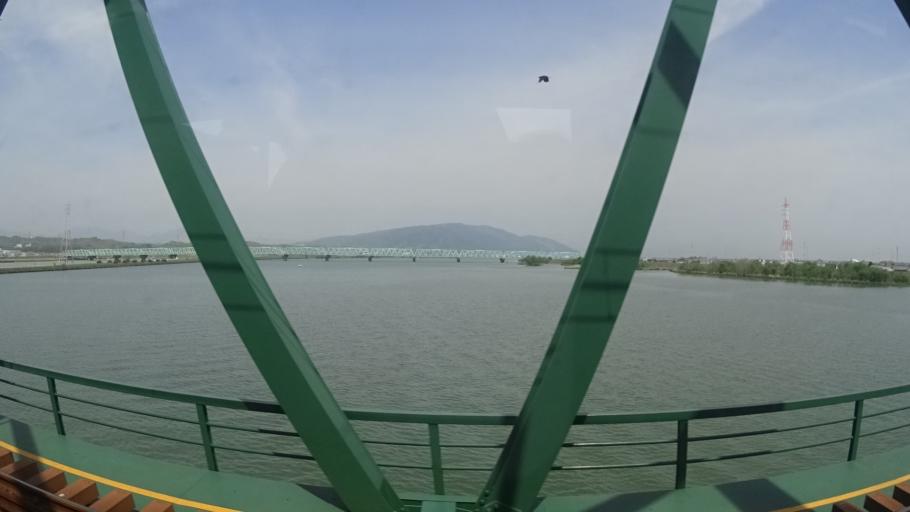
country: JP
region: Aichi
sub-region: Tsushima-shi
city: Tsushima
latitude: 35.0928
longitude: 136.6860
